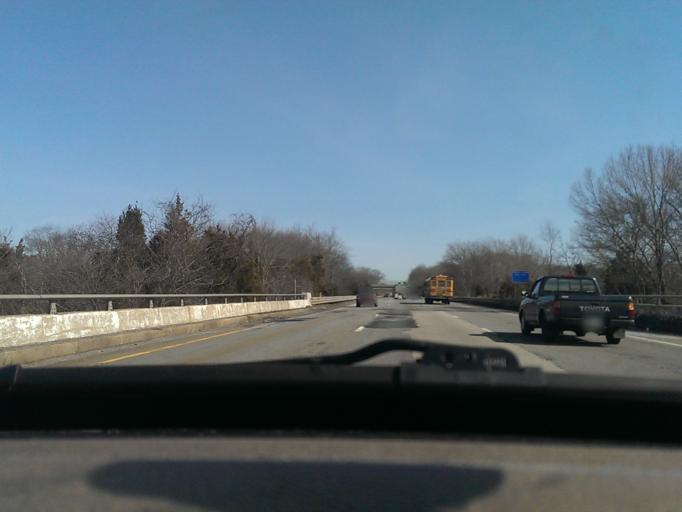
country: US
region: Rhode Island
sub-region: Bristol County
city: Barrington
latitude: 41.7788
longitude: -71.2797
